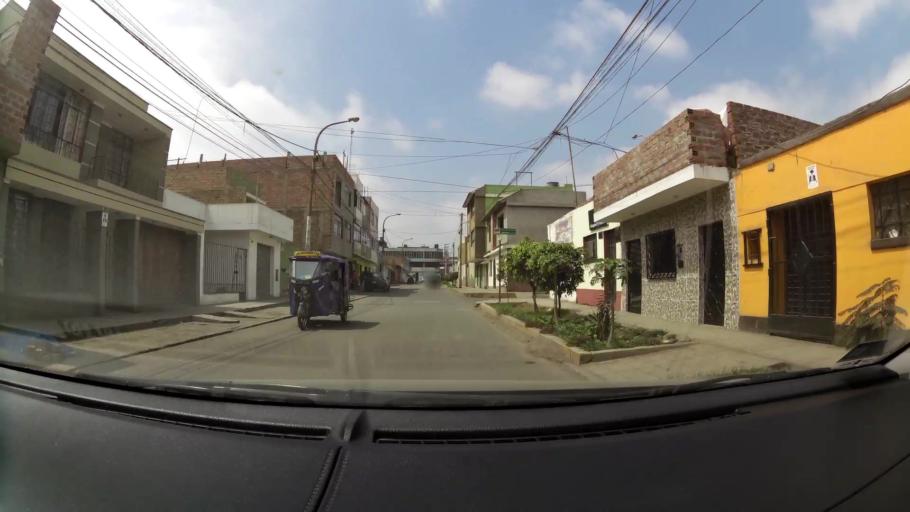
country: PE
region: Lima
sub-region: Provincia de Huaral
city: Huaral
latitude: -11.4949
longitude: -77.2115
